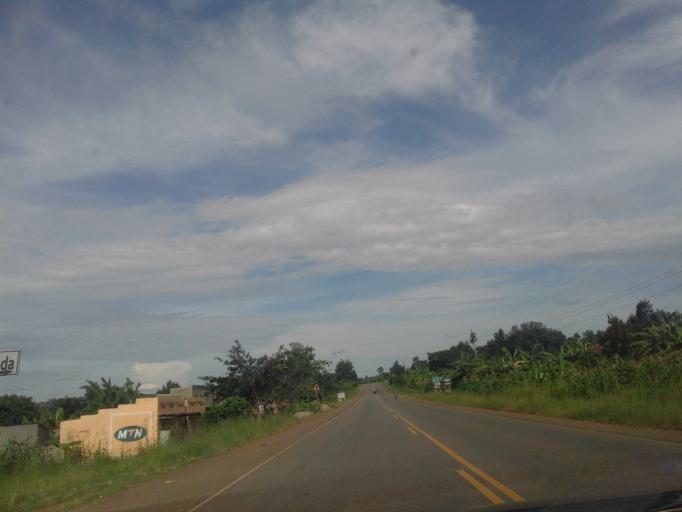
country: UG
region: Central Region
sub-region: Lwengo District
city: Lwengo
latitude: -0.3684
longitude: 31.5337
